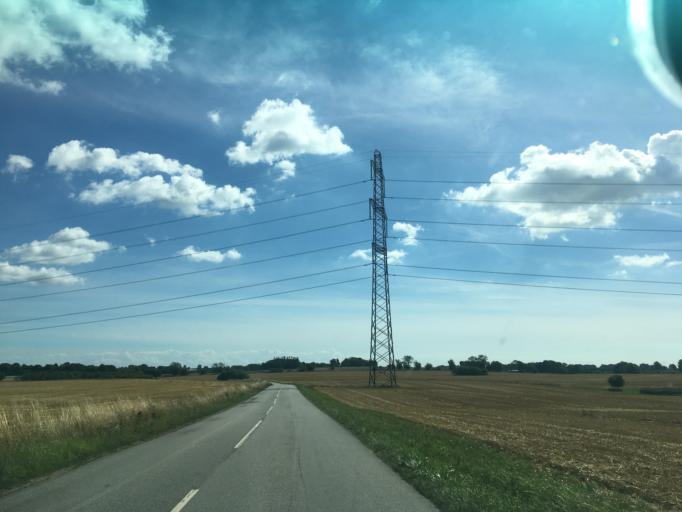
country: DK
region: Zealand
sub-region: Solrod Kommune
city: Solrod
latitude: 55.5656
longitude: 12.1817
